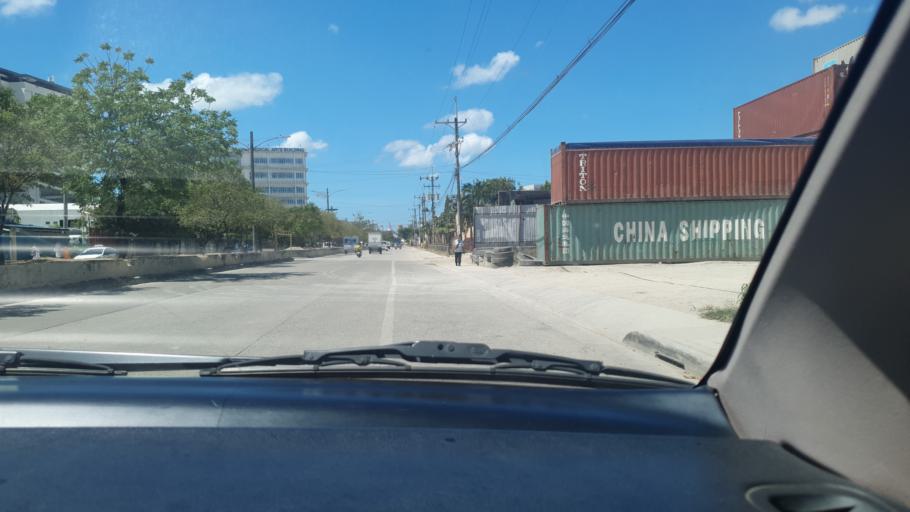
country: PH
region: Central Visayas
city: Mandaue City
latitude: 10.3228
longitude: 123.9307
